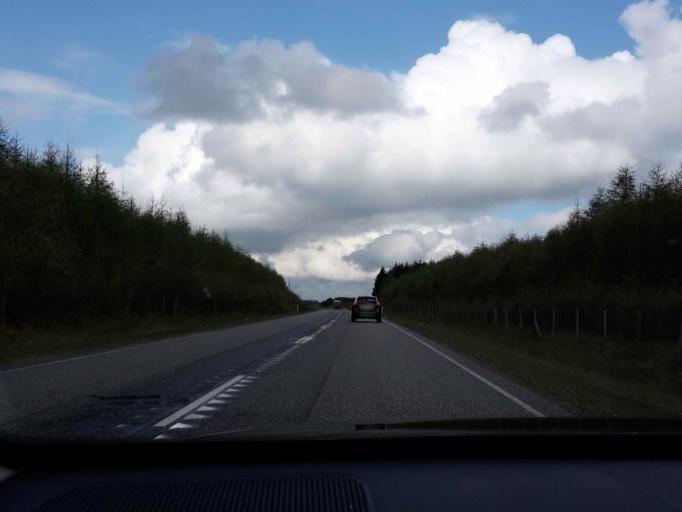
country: DK
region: South Denmark
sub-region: Billund Kommune
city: Billund
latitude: 55.7477
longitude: 9.1703
